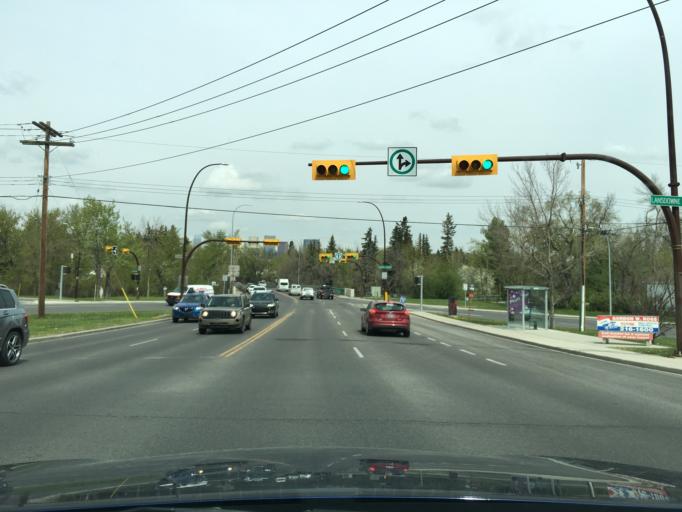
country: CA
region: Alberta
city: Calgary
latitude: 51.0165
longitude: -114.0785
